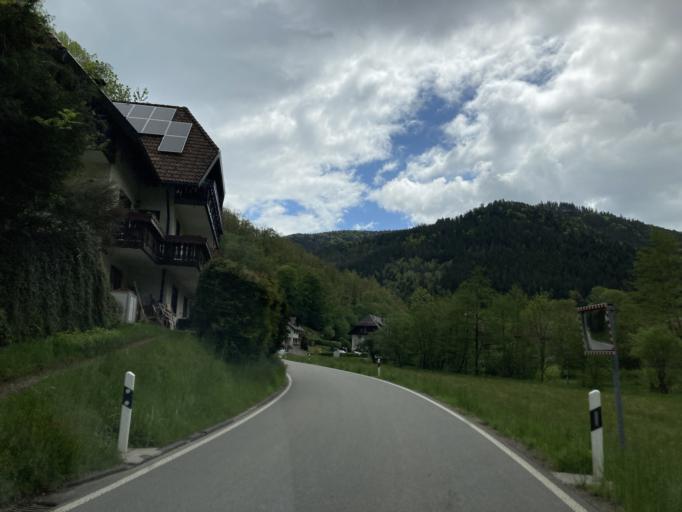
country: DE
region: Baden-Wuerttemberg
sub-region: Freiburg Region
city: Muhlenbach
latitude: 48.2058
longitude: 8.1577
